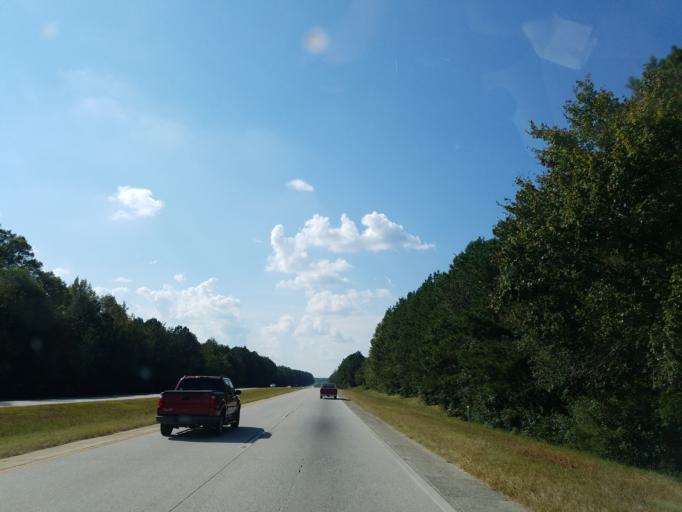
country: US
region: Georgia
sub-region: Oconee County
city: Bogart
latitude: 33.9335
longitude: -83.5343
